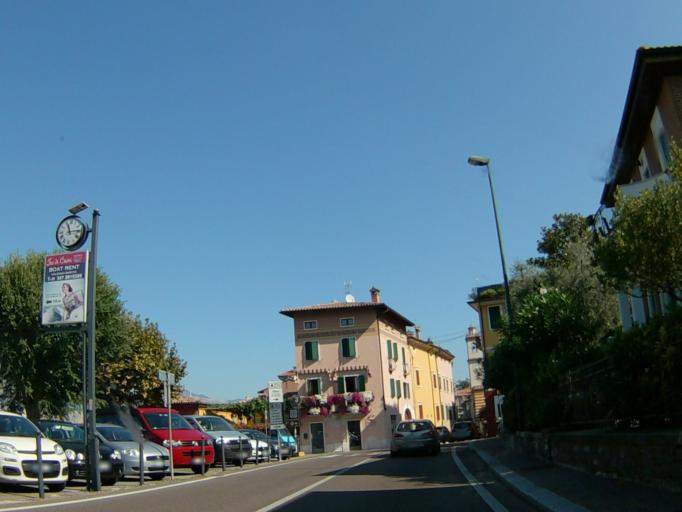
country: IT
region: Veneto
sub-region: Provincia di Verona
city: Brenzone
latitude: 45.6863
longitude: 10.7494
